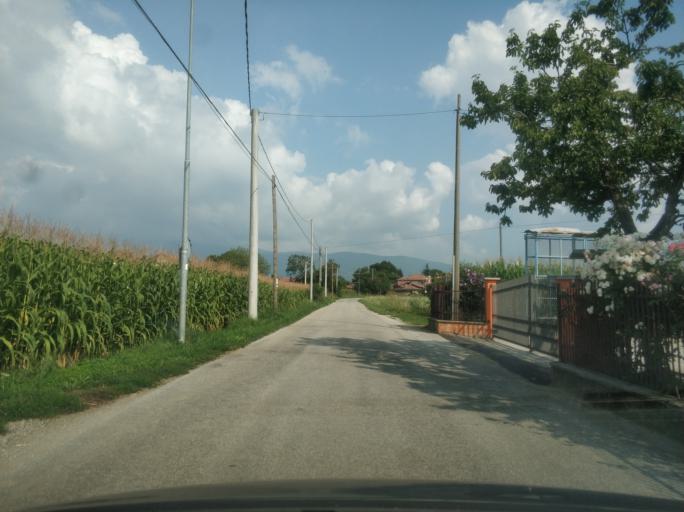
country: IT
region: Piedmont
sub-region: Provincia di Cuneo
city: Caraglio
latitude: 44.4345
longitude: 7.4316
